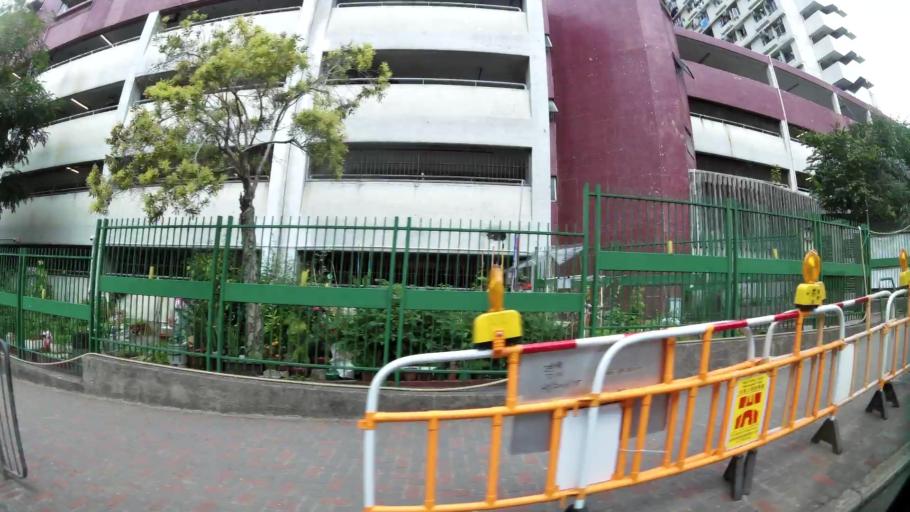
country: HK
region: Kowloon City
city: Kowloon
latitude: 22.3190
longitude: 114.2273
